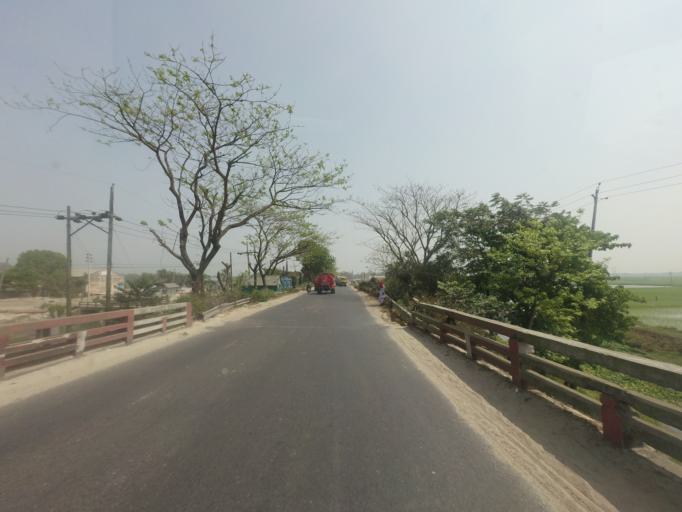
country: BD
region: Dhaka
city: Bhairab Bazar
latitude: 24.0380
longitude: 91.0248
